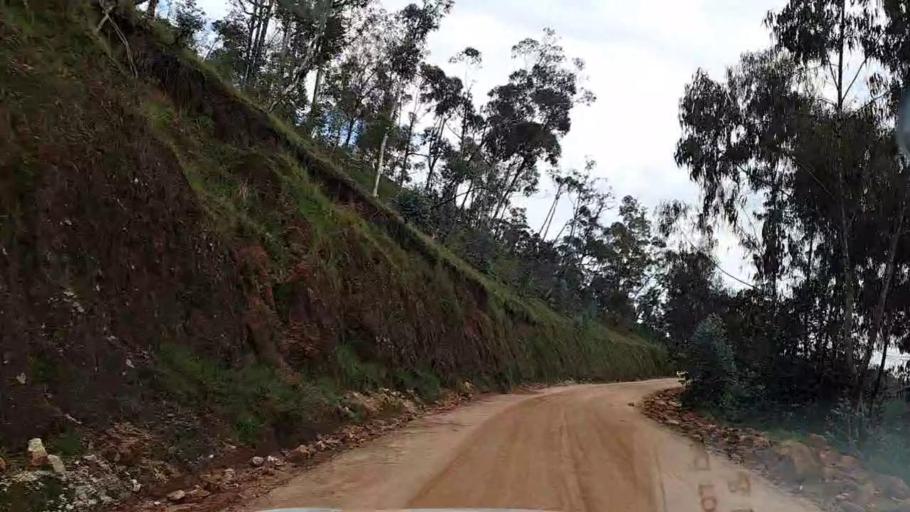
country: RW
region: Southern Province
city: Nzega
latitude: -2.3873
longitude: 29.4510
